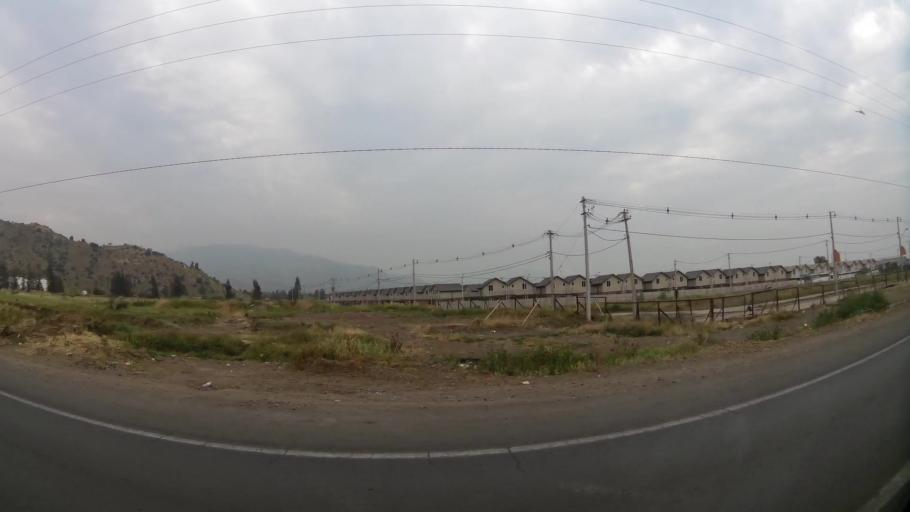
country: CL
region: Santiago Metropolitan
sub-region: Provincia de Chacabuco
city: Chicureo Abajo
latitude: -33.1940
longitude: -70.6660
